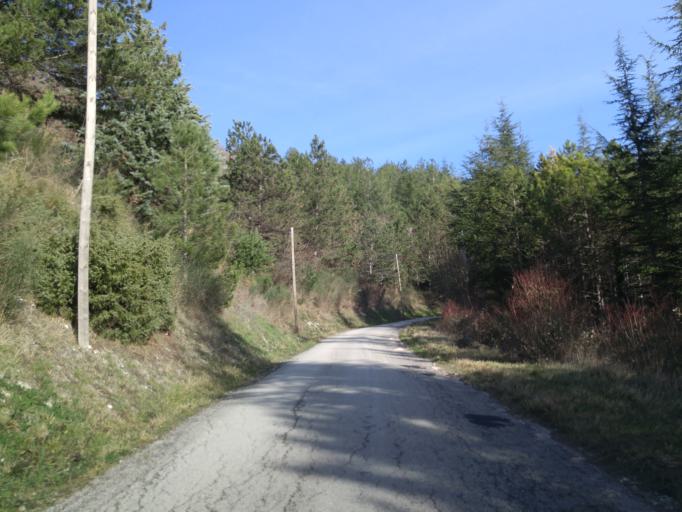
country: IT
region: The Marches
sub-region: Provincia di Pesaro e Urbino
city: Fermignano
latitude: 43.6779
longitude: 12.6754
